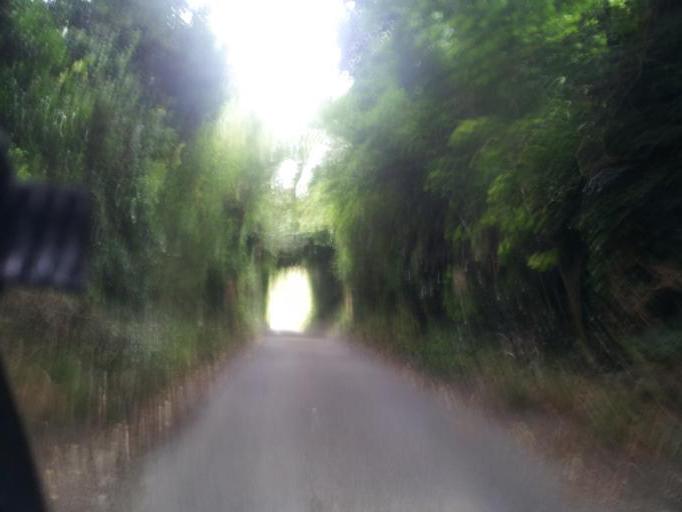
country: GB
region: England
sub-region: Kent
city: Meopham
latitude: 51.3607
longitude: 0.3800
